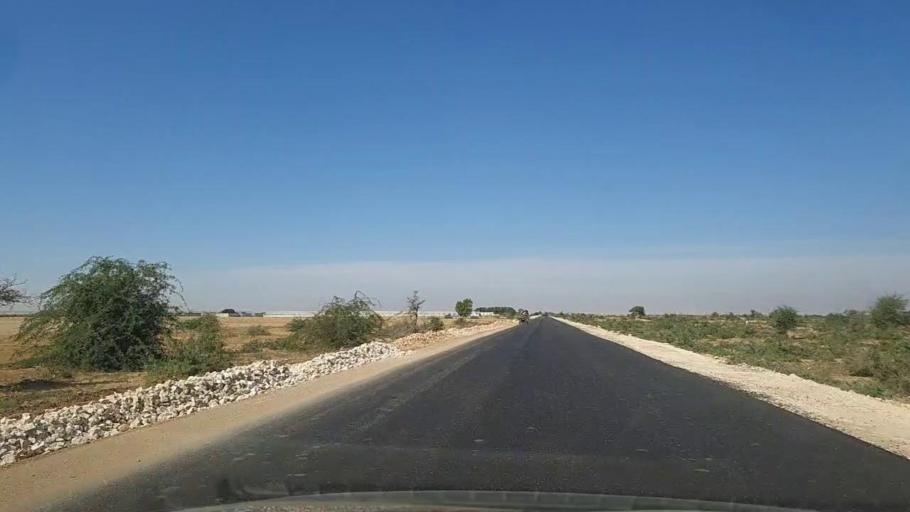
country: PK
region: Sindh
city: Kotri
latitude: 25.2527
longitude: 68.2267
